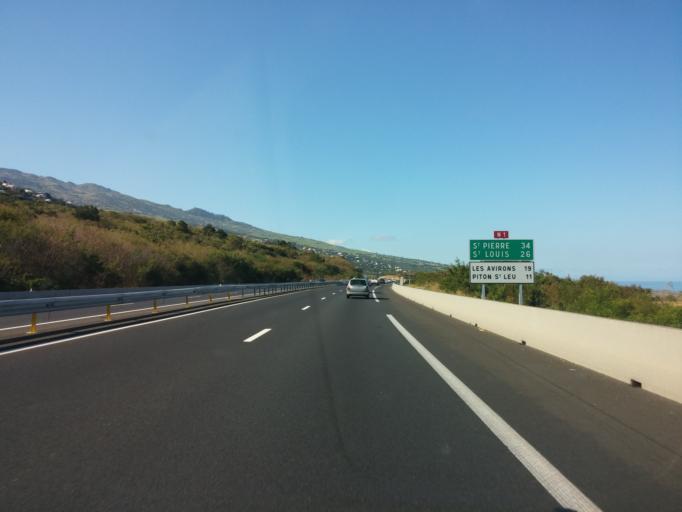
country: RE
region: Reunion
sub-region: Reunion
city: Saint-Leu
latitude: -21.1477
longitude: 55.2889
